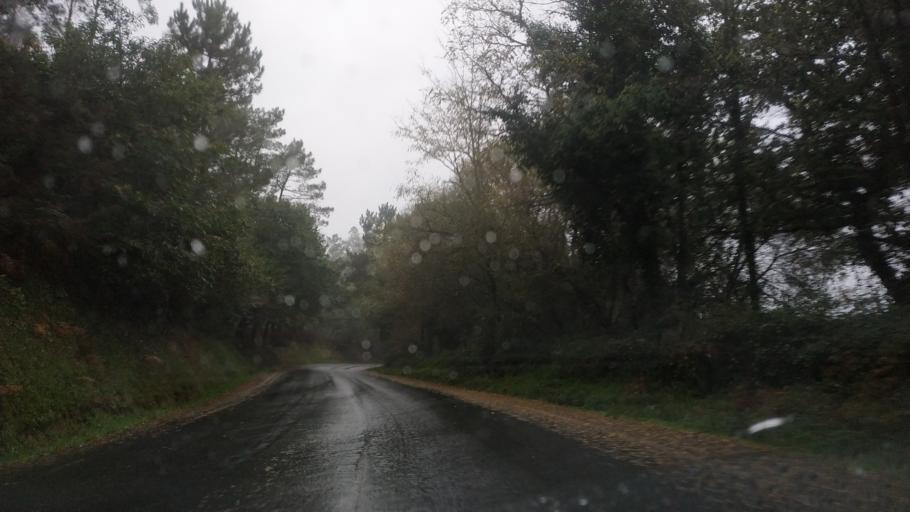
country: ES
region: Galicia
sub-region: Provincia da Coruna
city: Negreira
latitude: 42.9087
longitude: -8.7482
